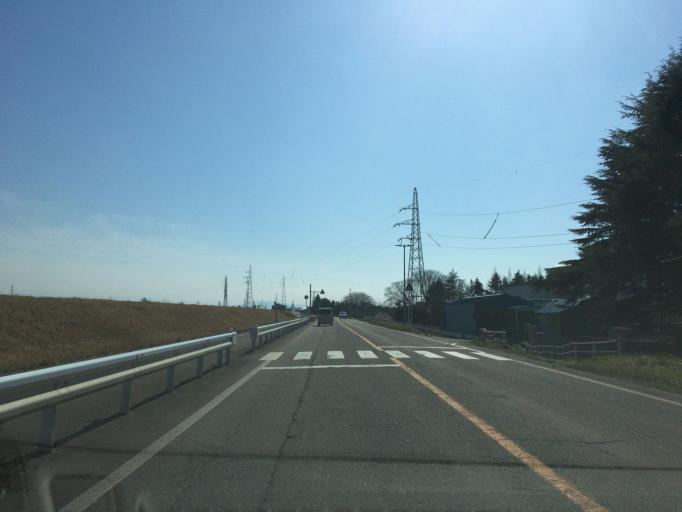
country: JP
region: Toyama
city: Nishishinminato
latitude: 36.7859
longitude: 137.0649
